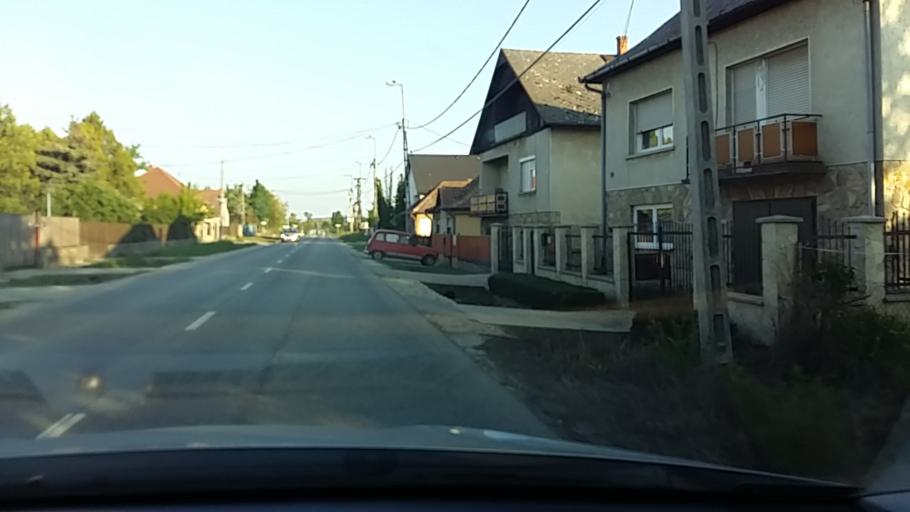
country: HU
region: Pest
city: Orbottyan
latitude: 47.6770
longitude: 19.2677
